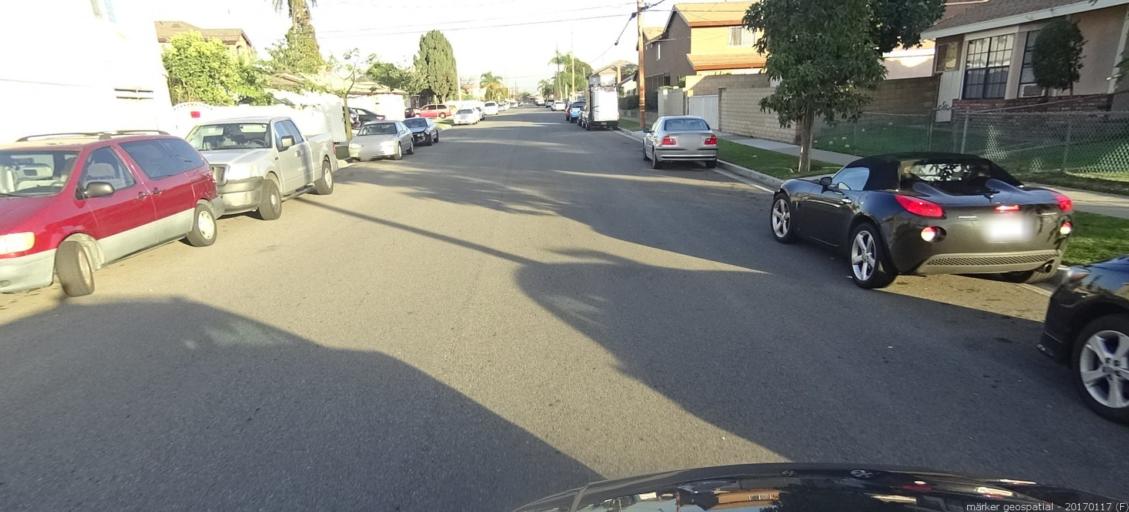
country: US
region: California
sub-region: Orange County
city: Midway City
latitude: 33.7466
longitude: -117.9831
